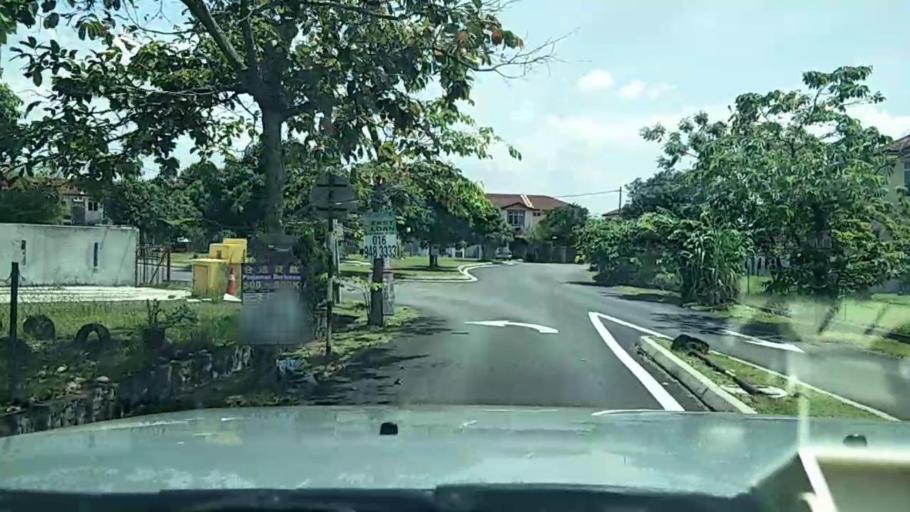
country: MY
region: Putrajaya
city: Putrajaya
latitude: 2.9431
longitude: 101.6188
